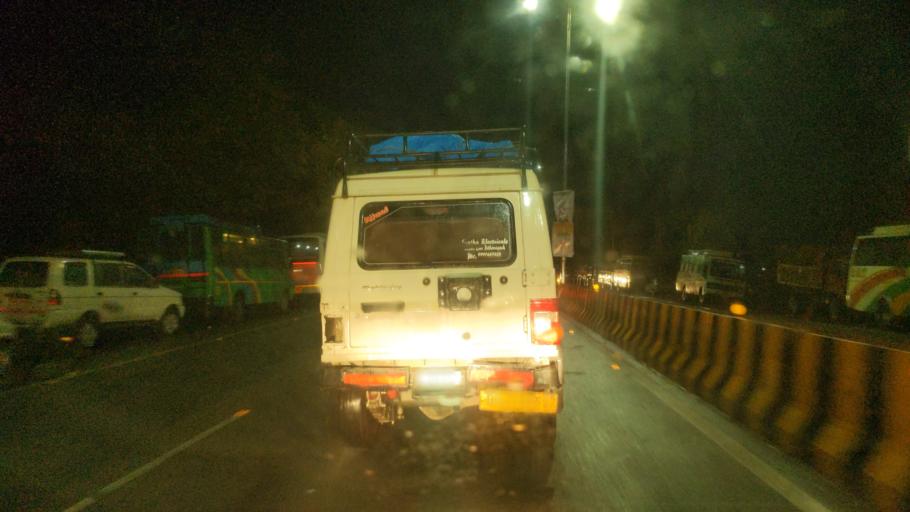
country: IN
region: Uttarakhand
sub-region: Naini Tal
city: Haldwani
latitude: 29.2588
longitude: 79.5431
